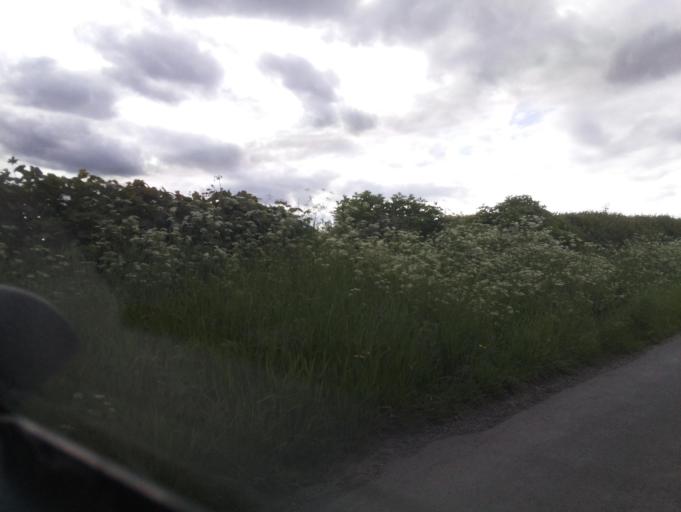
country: GB
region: England
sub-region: Gloucestershire
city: Chipping Campden
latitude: 52.0370
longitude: -1.7273
